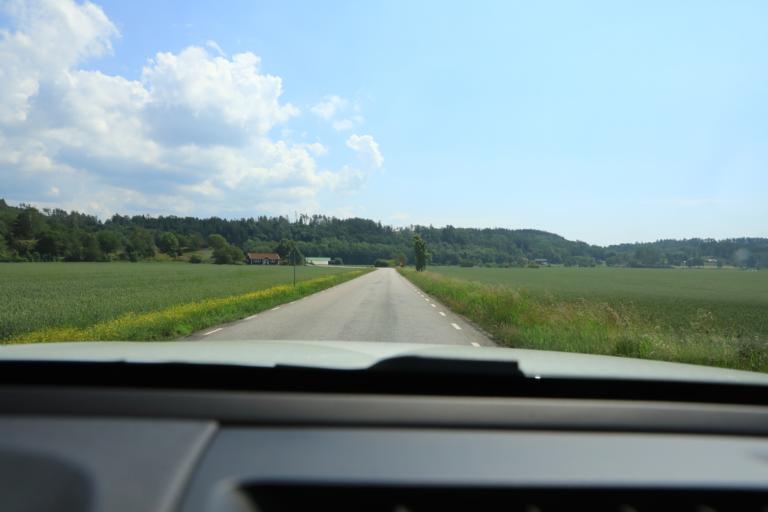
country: SE
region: Halland
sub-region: Varbergs Kommun
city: Veddige
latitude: 57.2057
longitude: 12.3225
